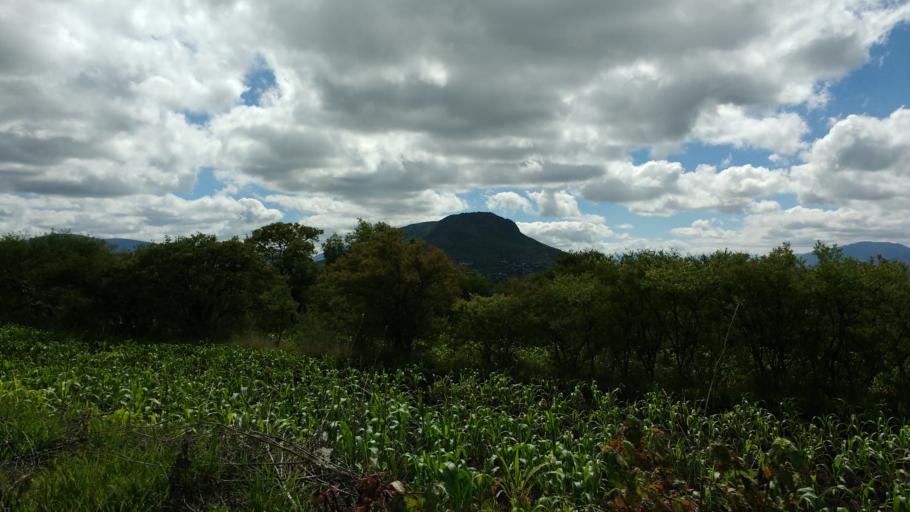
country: MX
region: Hidalgo
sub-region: Tezontepec de Aldama
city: Tenango
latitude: 20.2480
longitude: -99.2764
